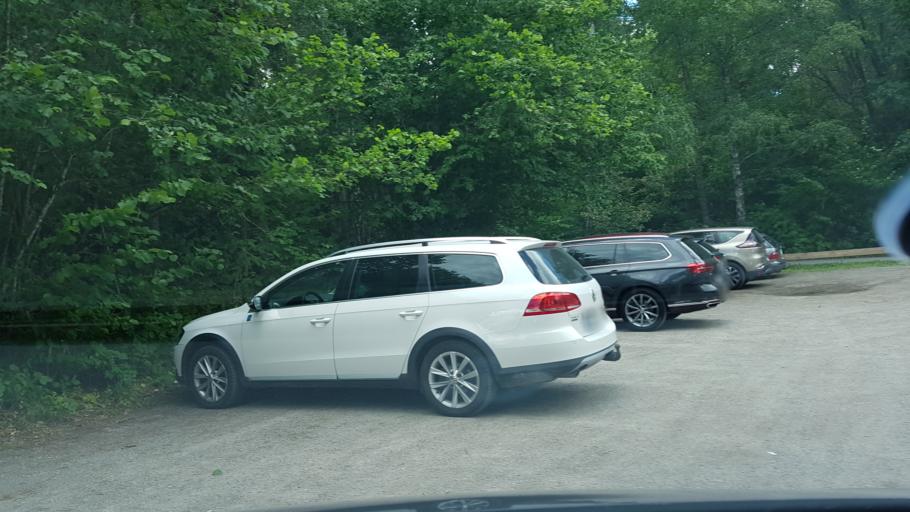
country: SE
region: Stockholm
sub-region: Upplands-Bro Kommun
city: Kungsaengen
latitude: 59.5028
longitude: 17.8109
